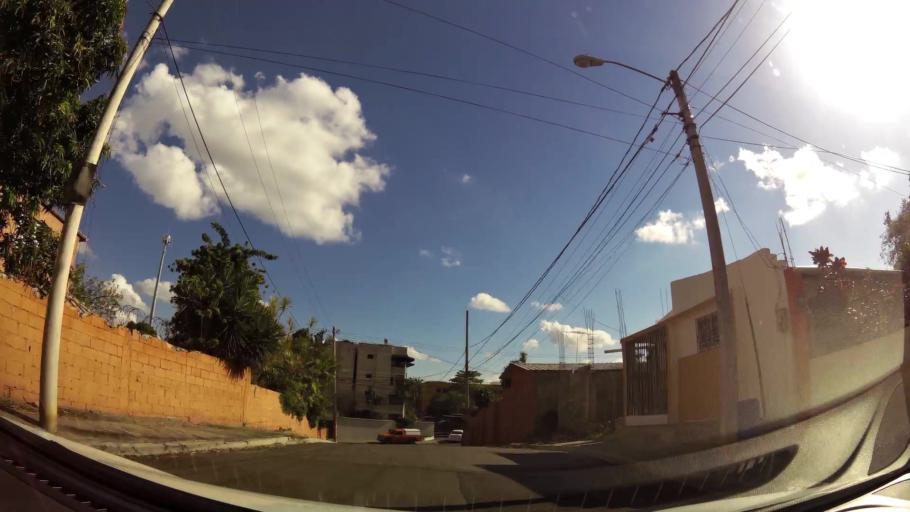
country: DO
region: Santiago
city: Santiago de los Caballeros
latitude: 19.4515
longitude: -70.6793
